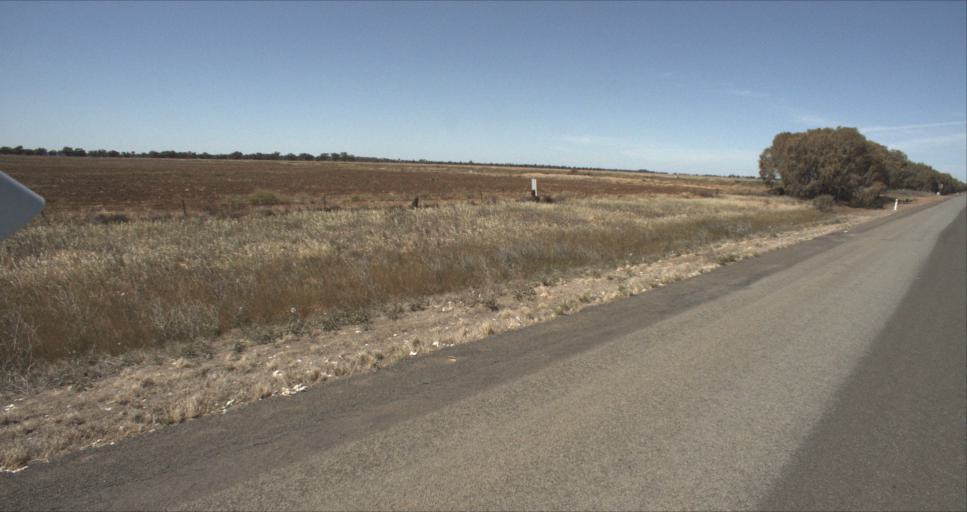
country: AU
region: New South Wales
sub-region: Leeton
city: Leeton
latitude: -34.4808
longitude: 146.2906
